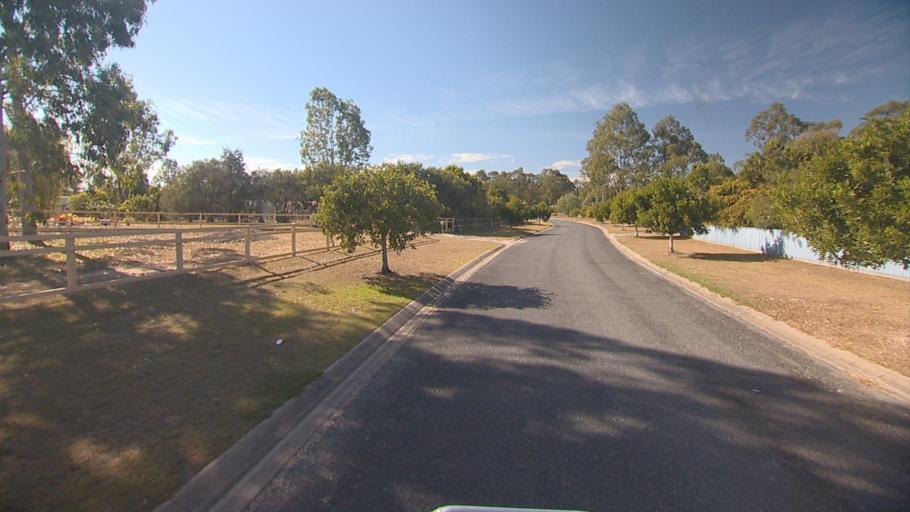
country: AU
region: Queensland
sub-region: Logan
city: North Maclean
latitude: -27.8009
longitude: 152.9680
